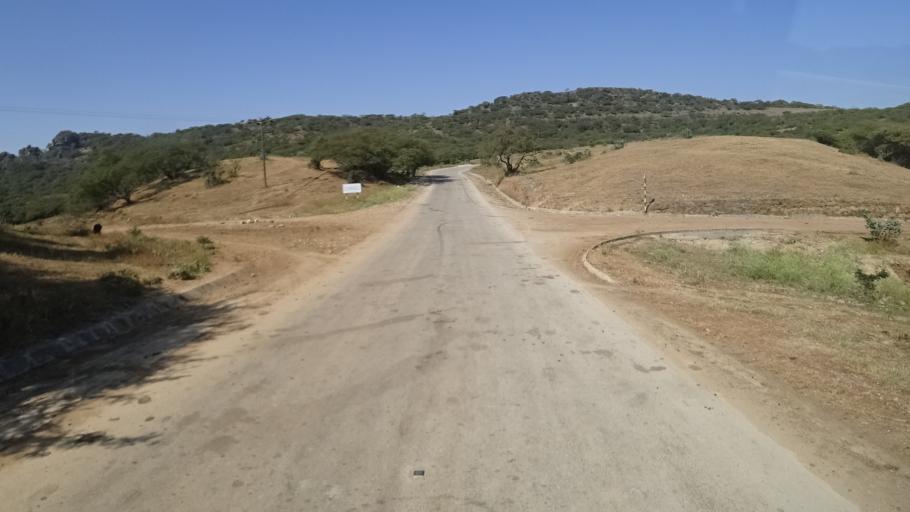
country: OM
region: Zufar
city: Salalah
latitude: 17.0668
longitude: 54.5977
